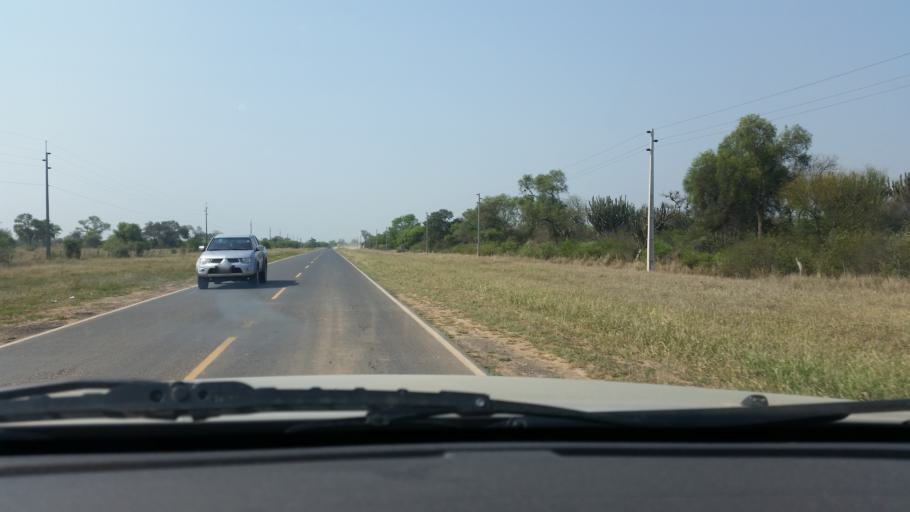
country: PY
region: Boqueron
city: Filadelfia
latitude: -22.4221
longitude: -60.0285
